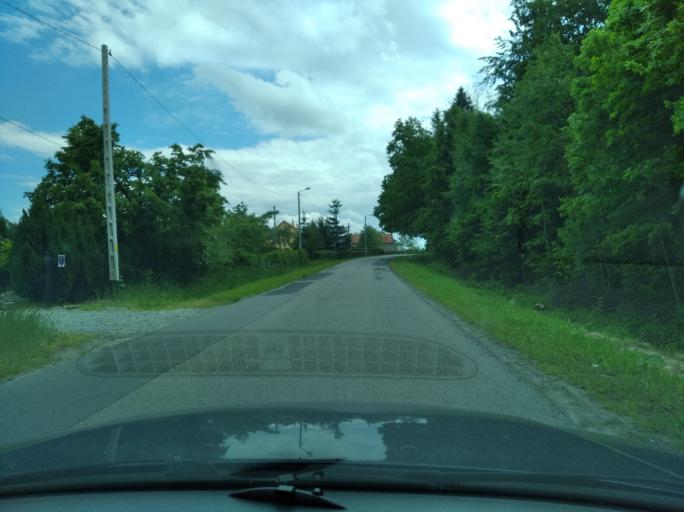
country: PL
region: Subcarpathian Voivodeship
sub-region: Powiat ropczycko-sedziszowski
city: Ropczyce
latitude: 50.0144
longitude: 21.6109
